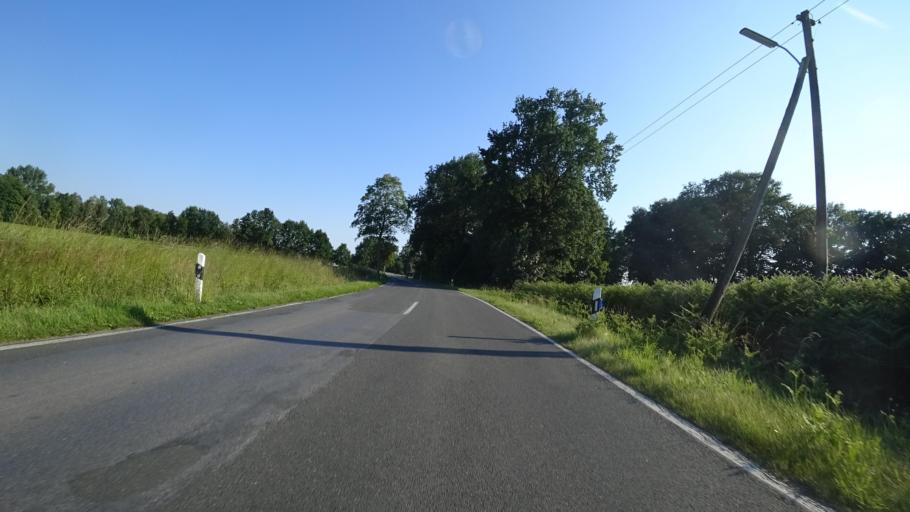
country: DE
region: North Rhine-Westphalia
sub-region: Regierungsbezirk Detmold
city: Steinhagen
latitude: 51.9568
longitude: 8.4140
